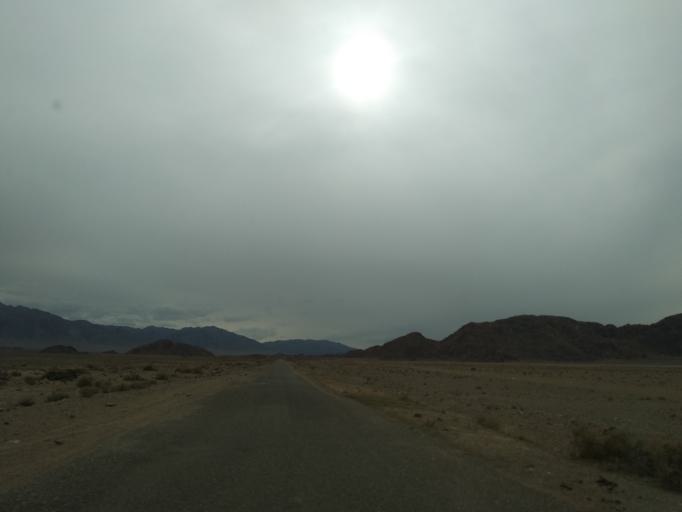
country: KG
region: Ysyk-Koel
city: Balykchy
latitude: 42.3170
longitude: 76.1600
